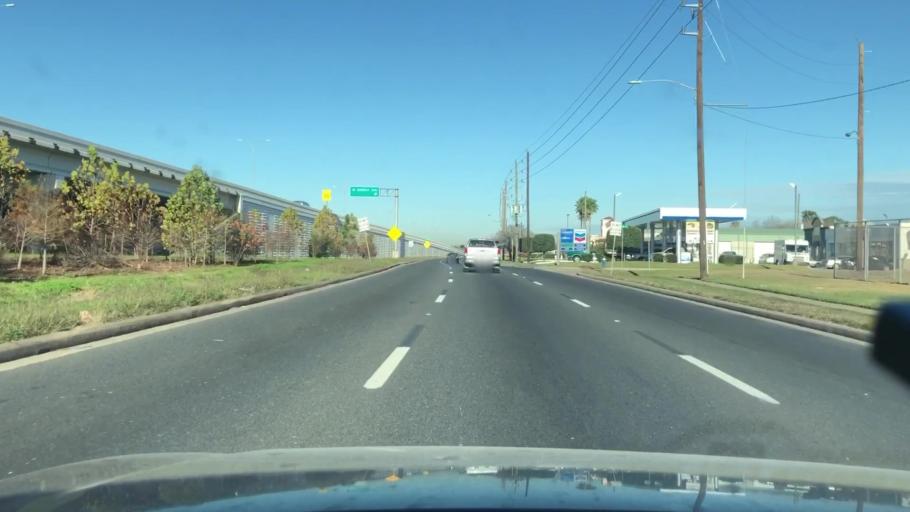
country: US
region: Texas
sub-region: Fort Bend County
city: Missouri City
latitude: 29.6452
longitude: -95.5395
